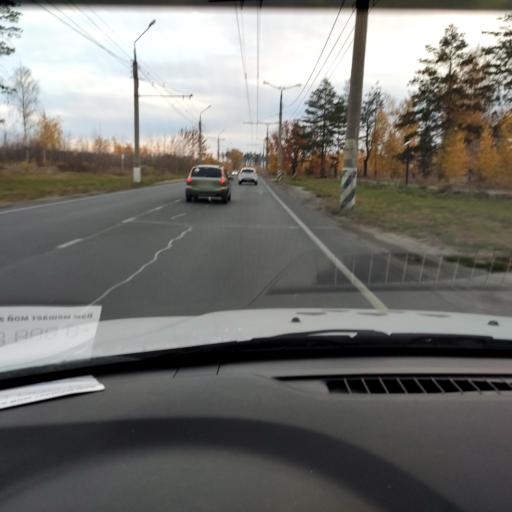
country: RU
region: Samara
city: Tol'yatti
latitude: 53.4864
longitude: 49.3818
